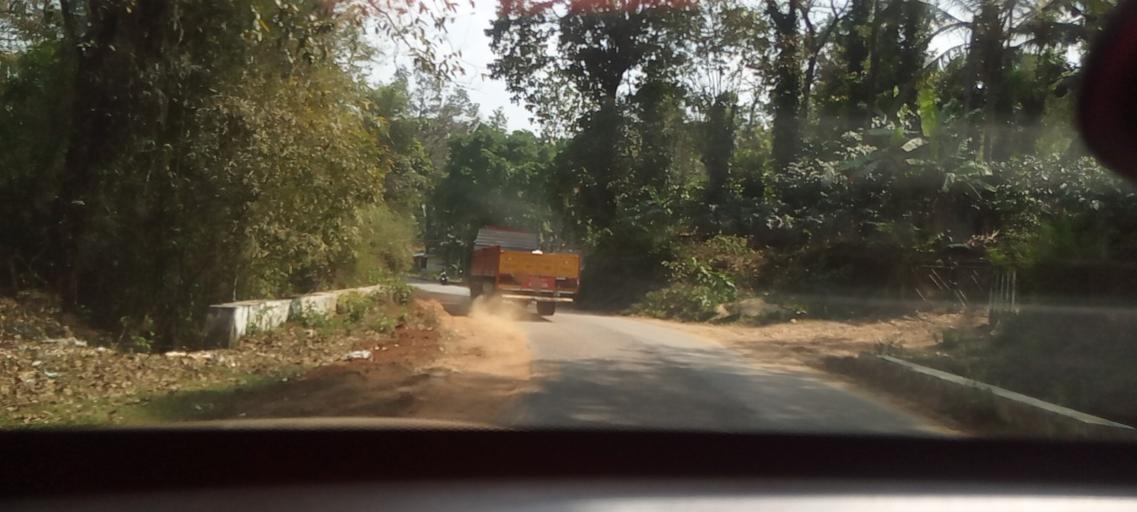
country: IN
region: Karnataka
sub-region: Chikmagalur
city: Mudigere
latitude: 13.3238
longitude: 75.5630
